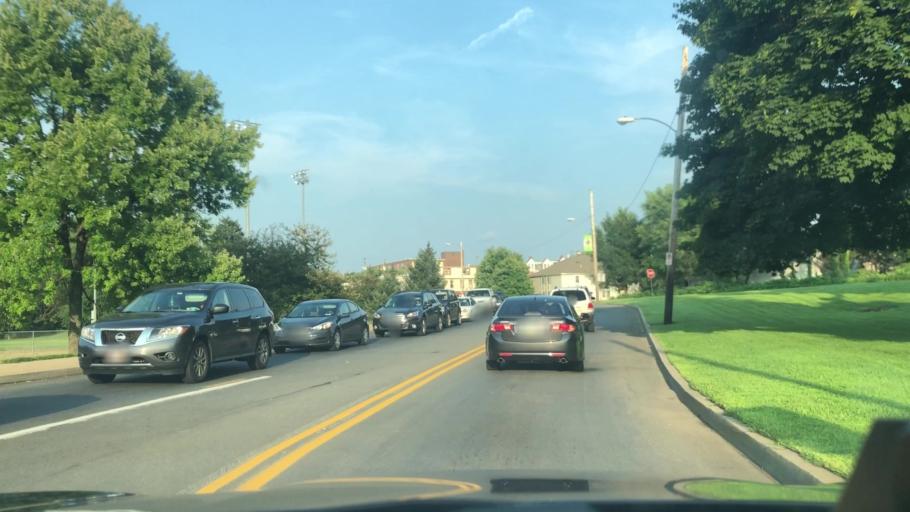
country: US
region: Pennsylvania
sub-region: Lehigh County
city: Fullerton
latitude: 40.6176
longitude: -75.4769
